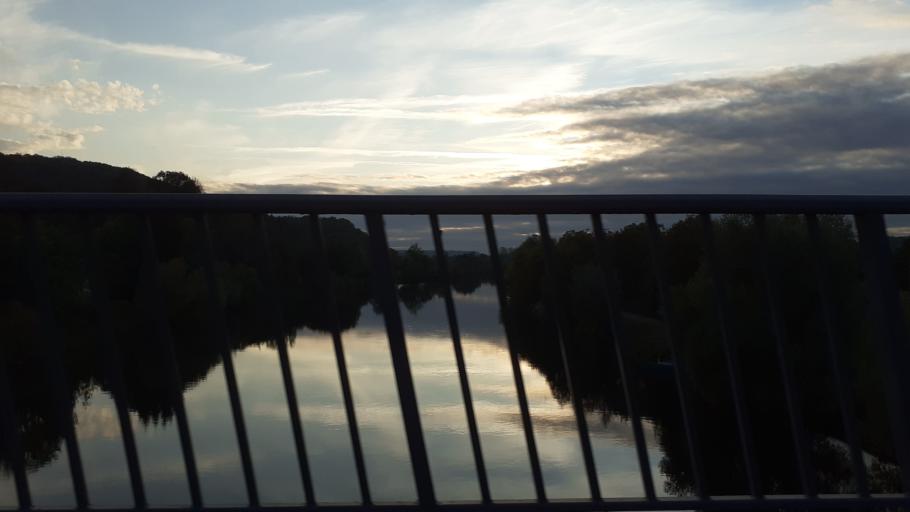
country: FR
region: Franche-Comte
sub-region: Departement du Doubs
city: Novillars
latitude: 47.2857
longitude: 6.1491
